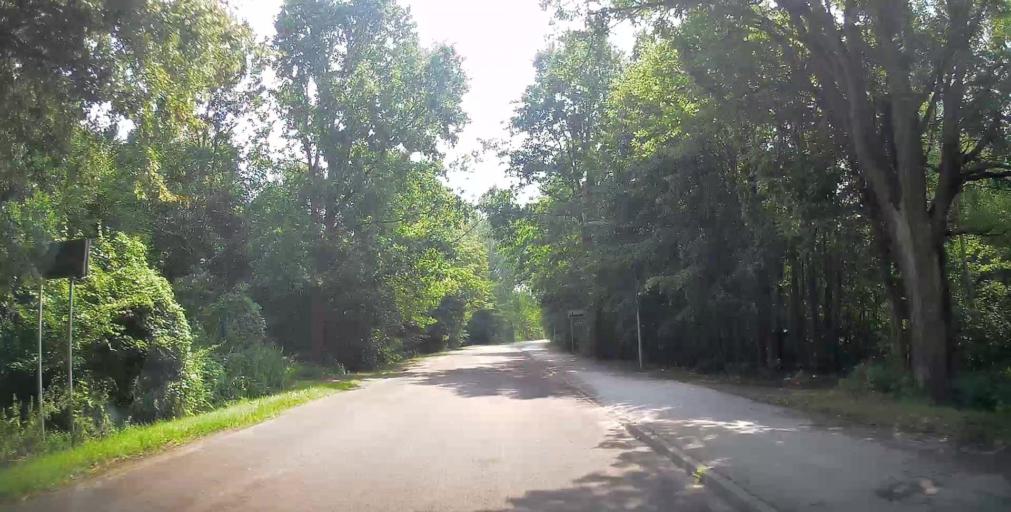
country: PL
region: Masovian Voivodeship
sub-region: Powiat bialobrzeski
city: Bialobrzegi
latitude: 51.6340
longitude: 20.9535
